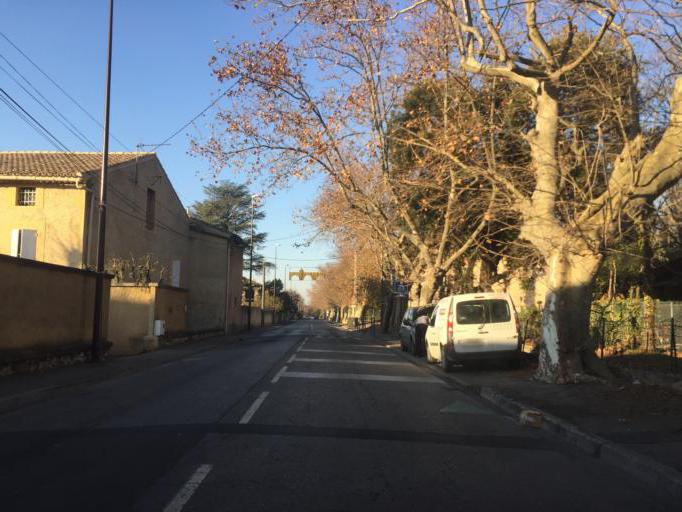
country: FR
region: Provence-Alpes-Cote d'Azur
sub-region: Departement du Vaucluse
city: Montfavet
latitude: 43.9363
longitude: 4.8716
